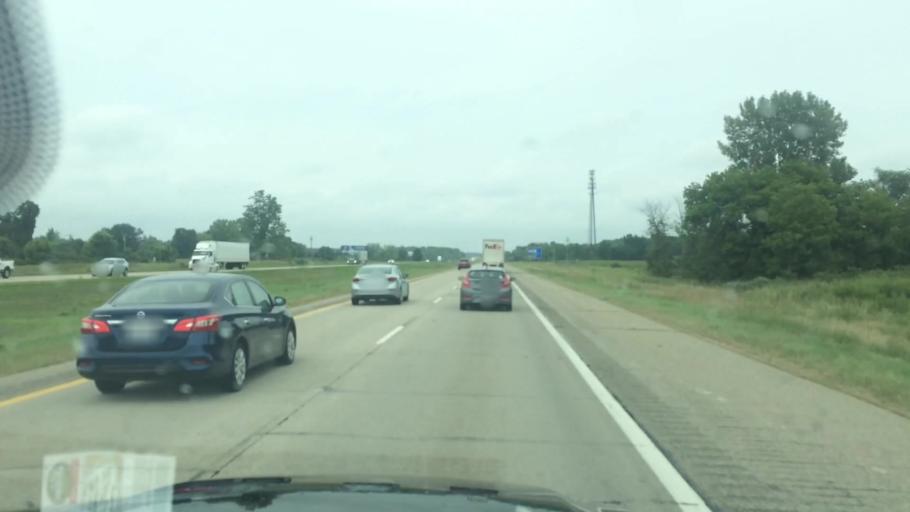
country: US
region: Michigan
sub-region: Eaton County
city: Potterville
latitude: 42.6096
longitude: -84.7624
